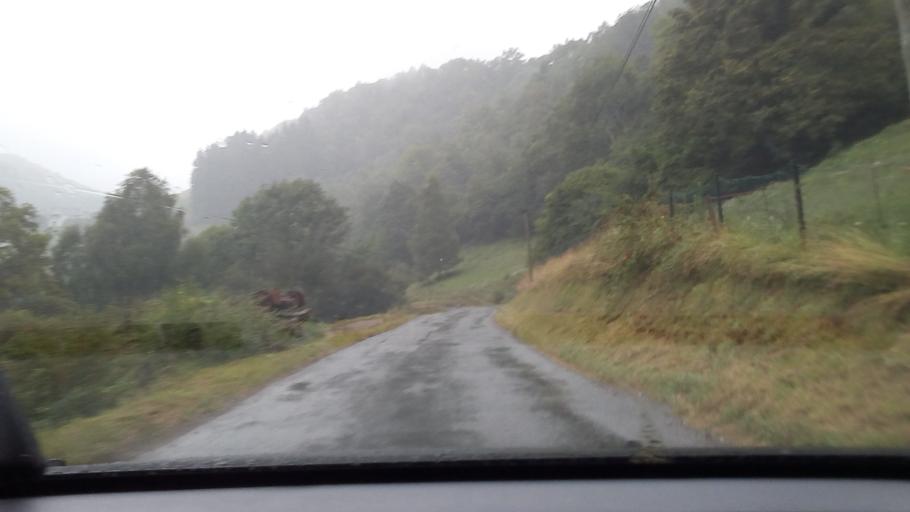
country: FR
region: Midi-Pyrenees
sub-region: Departement des Hautes-Pyrenees
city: Argeles-Gazost
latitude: 42.9861
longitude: -0.1322
